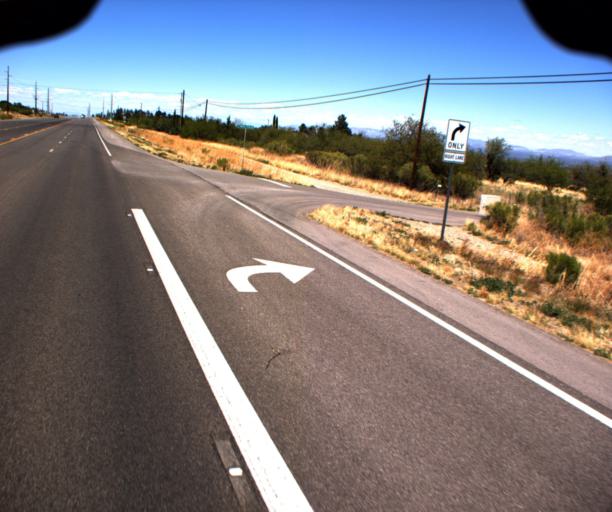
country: US
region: Arizona
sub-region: Cochise County
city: Sierra Vista Southeast
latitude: 31.4226
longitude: -110.2407
